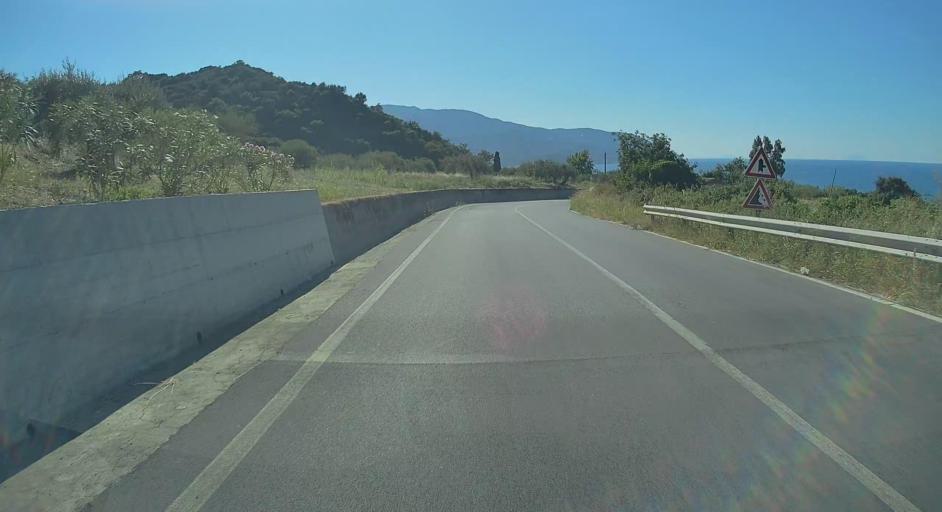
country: IT
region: Sicily
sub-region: Messina
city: Oliveri
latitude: 38.1411
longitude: 15.0169
